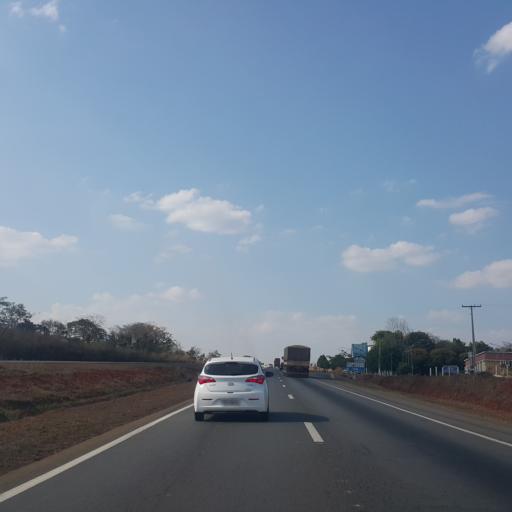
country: BR
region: Goias
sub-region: Abadiania
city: Abadiania
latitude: -16.2670
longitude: -48.7669
